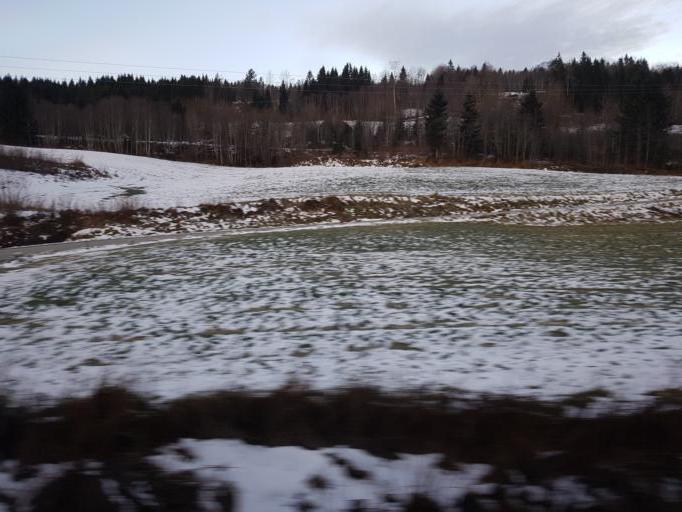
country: NO
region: Sor-Trondelag
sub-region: Midtre Gauldal
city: Storen
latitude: 62.9518
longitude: 10.1885
